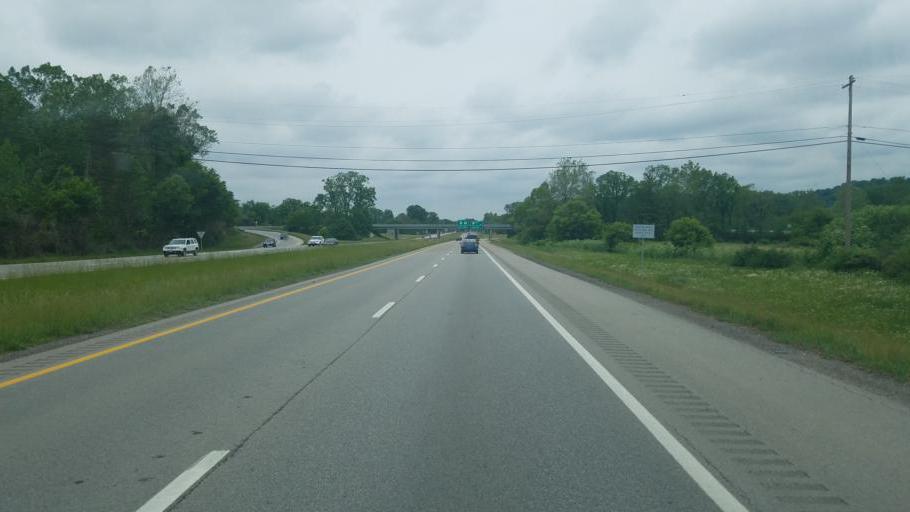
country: US
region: Ohio
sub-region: Licking County
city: Granville
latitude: 40.0603
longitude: -82.5257
